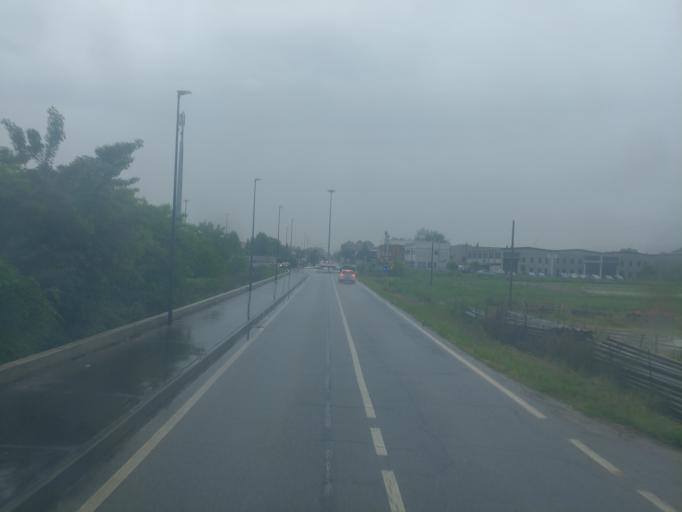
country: IT
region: Piedmont
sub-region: Provincia di Torino
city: La Loggia
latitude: 44.9452
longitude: 7.6698
